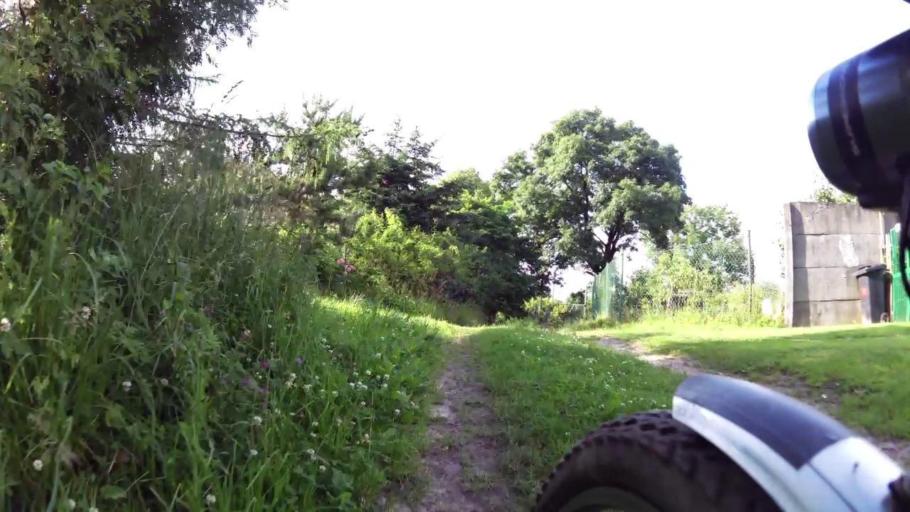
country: PL
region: West Pomeranian Voivodeship
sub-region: Powiat lobeski
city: Wegorzyno
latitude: 53.5412
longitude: 15.4563
